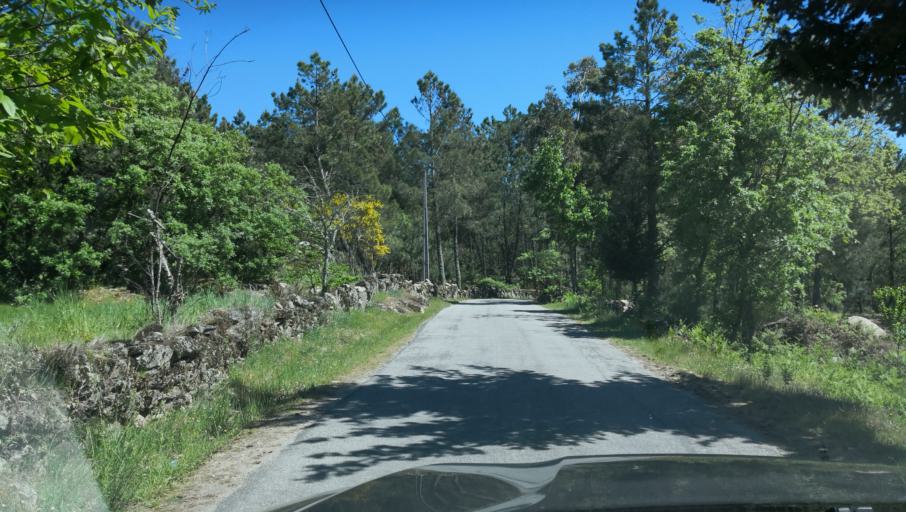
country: PT
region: Vila Real
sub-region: Vila Real
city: Vila Real
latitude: 41.2958
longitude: -7.6591
